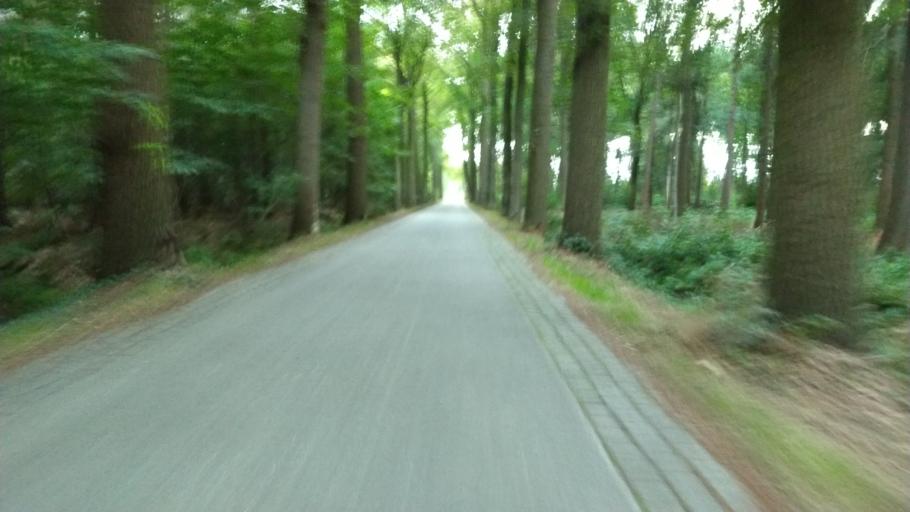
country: BE
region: Flanders
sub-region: Provincie Oost-Vlaanderen
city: Aalter
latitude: 51.0784
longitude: 3.4898
